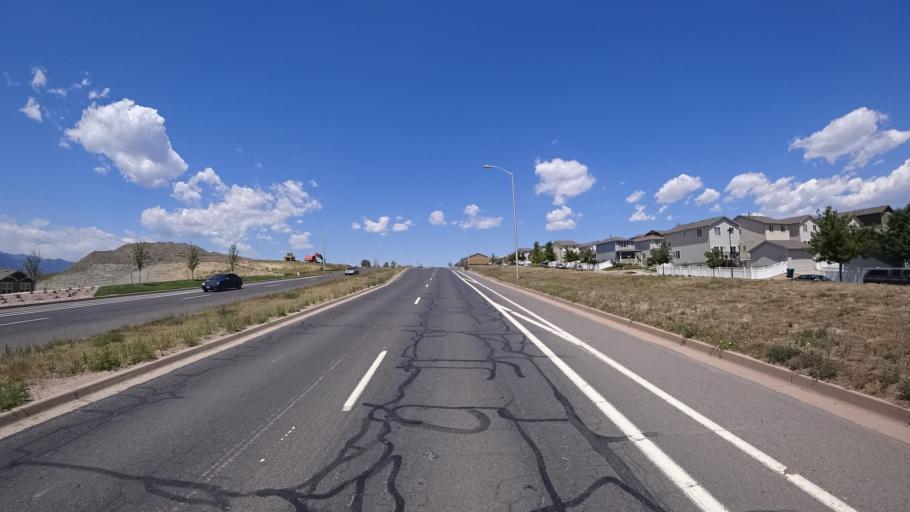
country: US
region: Colorado
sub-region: El Paso County
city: Stratmoor
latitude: 38.8039
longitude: -104.7859
